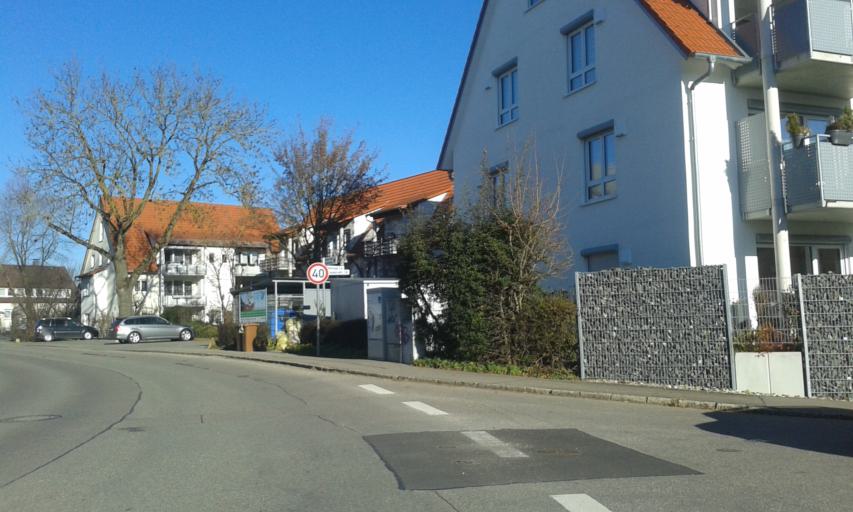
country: DE
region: Baden-Wuerttemberg
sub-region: Tuebingen Region
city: Dornstadt
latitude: 48.4342
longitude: 9.9690
